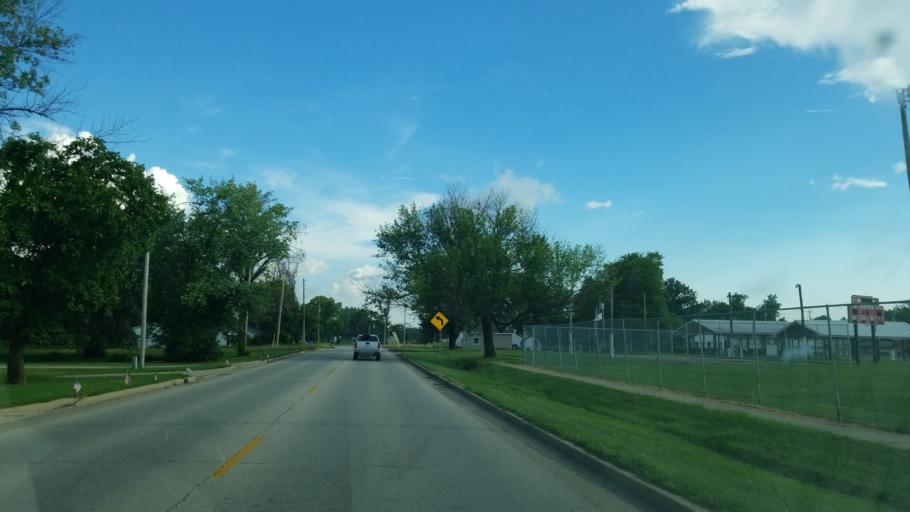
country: US
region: Illinois
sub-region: Marion County
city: Sandoval
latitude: 38.6096
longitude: -89.1153
